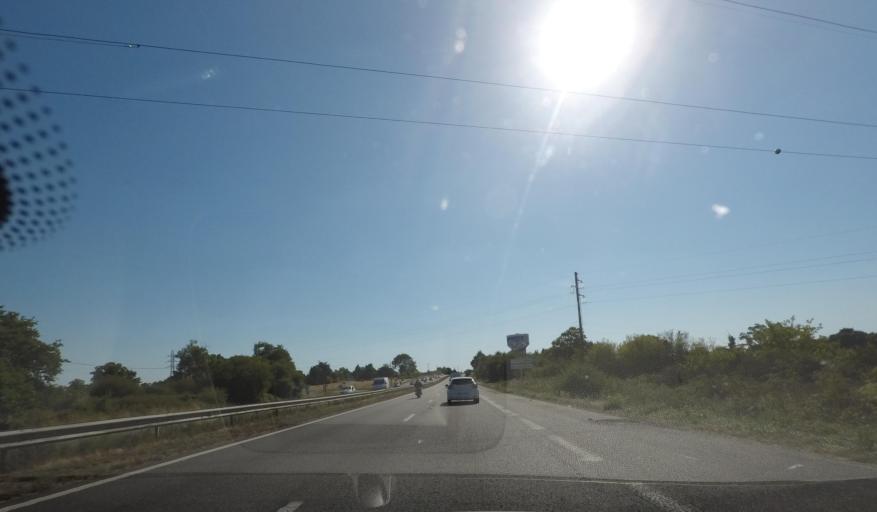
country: FR
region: Pays de la Loire
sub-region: Departement de la Loire-Atlantique
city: Montoir-de-Bretagne
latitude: 47.3329
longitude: -2.1198
